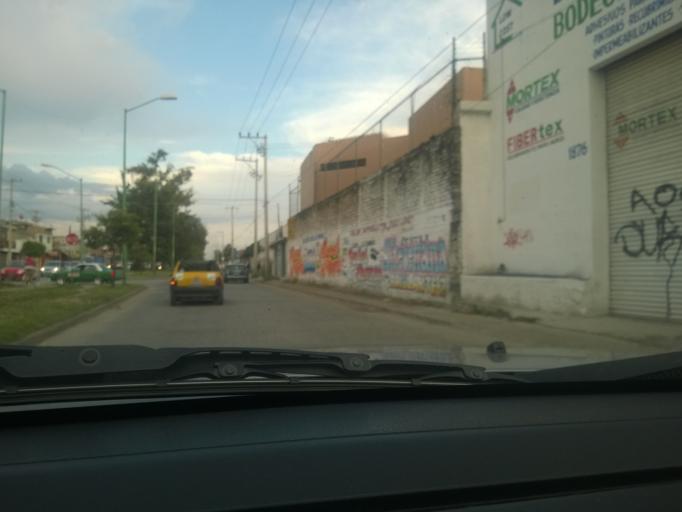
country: MX
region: Guanajuato
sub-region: Leon
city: Medina
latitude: 21.1170
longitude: -101.6370
